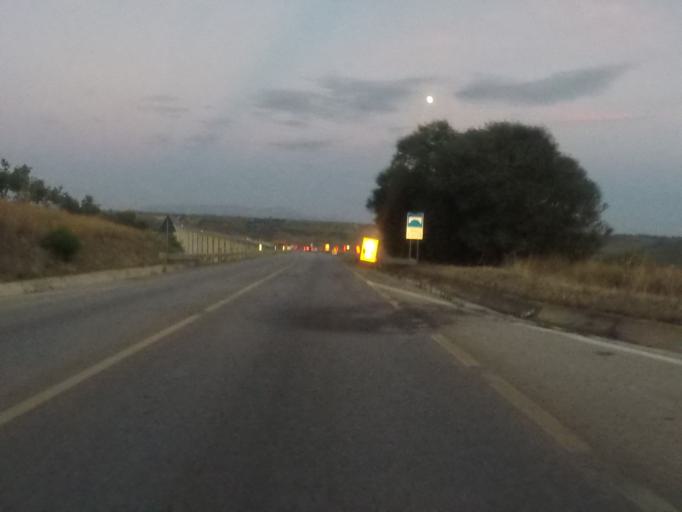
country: IT
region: Sicily
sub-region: Trapani
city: Marinella
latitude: 37.6335
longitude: 12.8756
